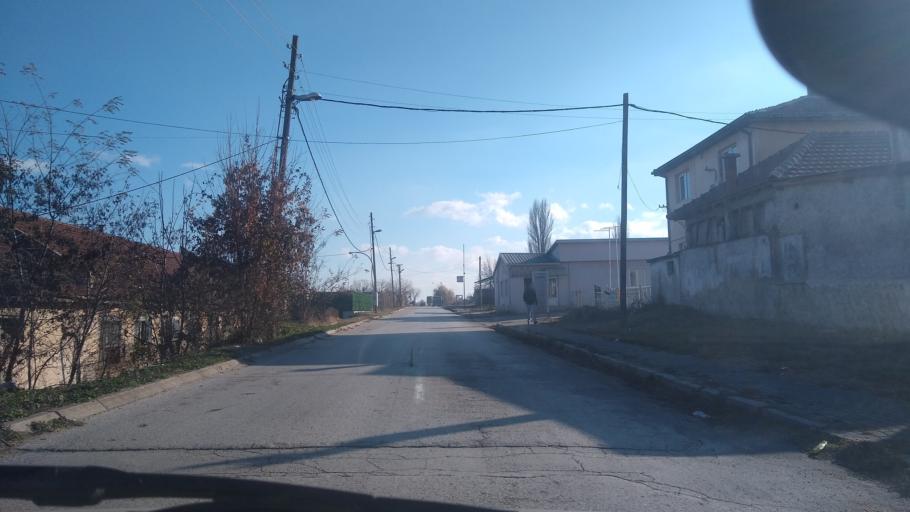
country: MK
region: Bitola
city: Bitola
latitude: 41.0139
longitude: 21.3455
